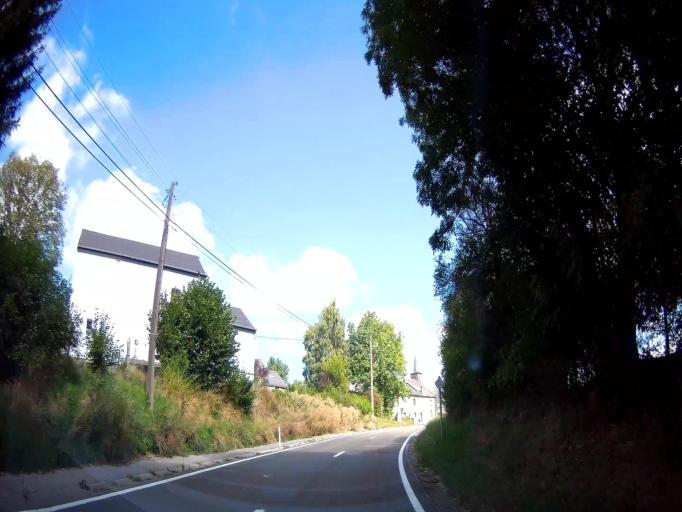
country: BE
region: Wallonia
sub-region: Province du Luxembourg
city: Bertogne
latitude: 50.0514
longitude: 5.6886
